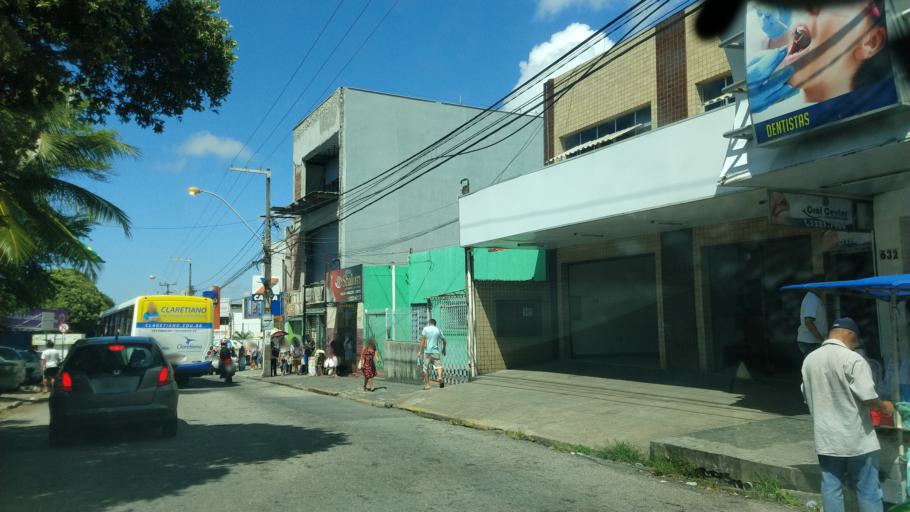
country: BR
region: Rio Grande do Norte
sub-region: Natal
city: Natal
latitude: -5.7995
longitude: -35.2165
